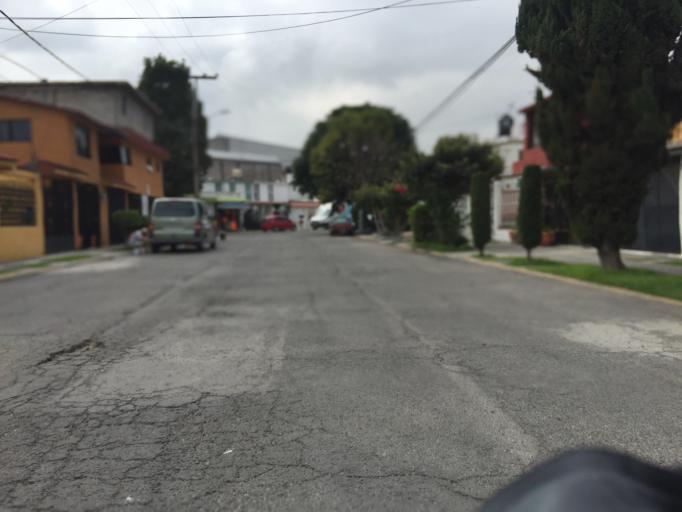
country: MX
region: Mexico
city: Cuautitlan Izcalli
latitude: 19.6686
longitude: -99.2061
